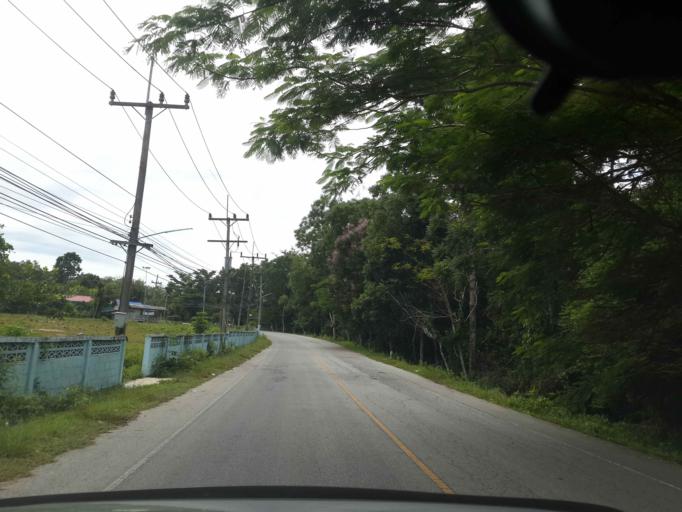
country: TH
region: Narathiwat
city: Rueso
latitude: 6.3838
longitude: 101.5155
